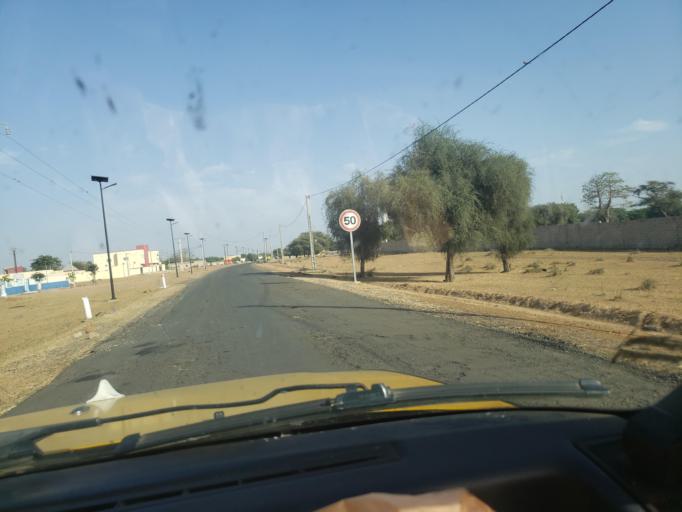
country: SN
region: Louga
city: Louga
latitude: 15.5128
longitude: -15.9955
